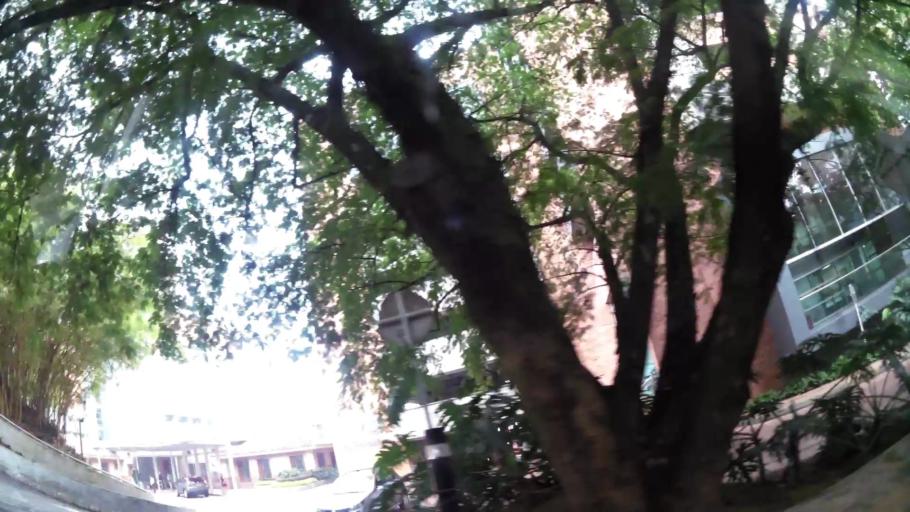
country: CO
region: Antioquia
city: Envigado
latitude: 6.1942
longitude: -75.5570
